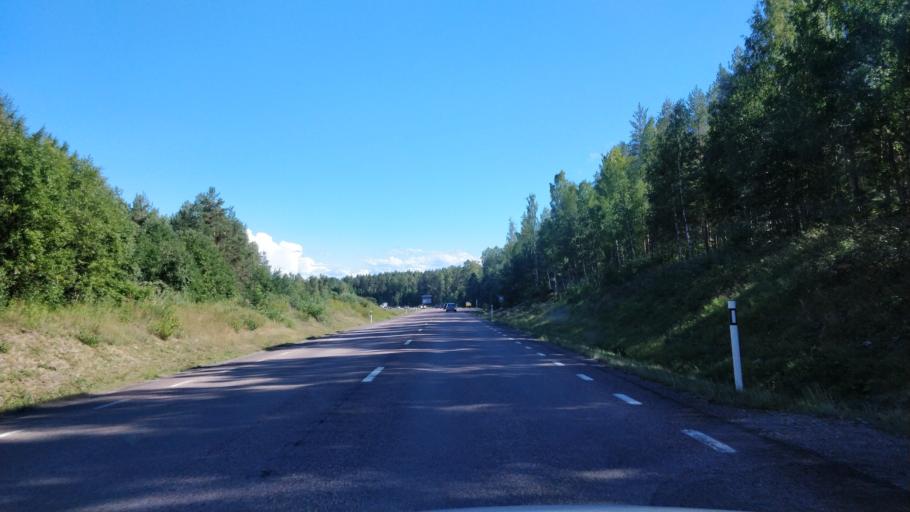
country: SE
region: Dalarna
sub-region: Faluns Kommun
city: Falun
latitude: 60.6340
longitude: 15.5915
